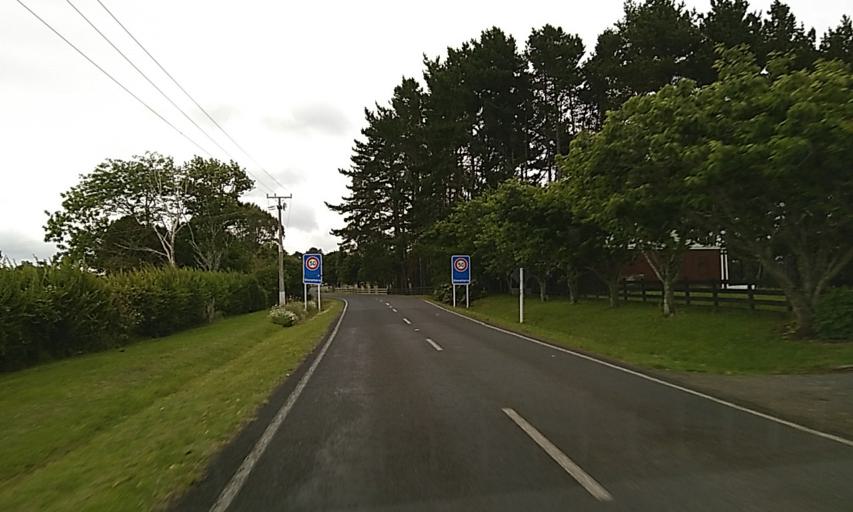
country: NZ
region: Auckland
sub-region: Auckland
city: Pukekohe East
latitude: -37.3234
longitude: 174.9183
